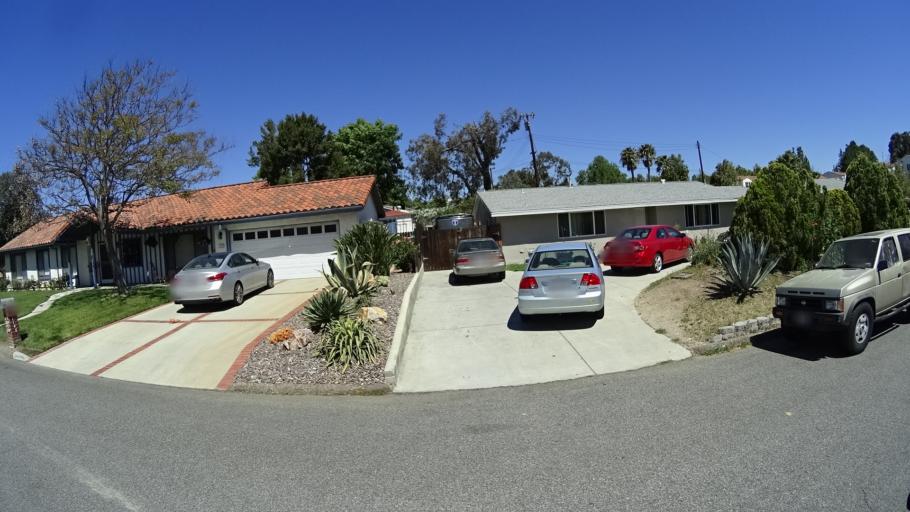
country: US
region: California
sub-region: Ventura County
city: Thousand Oaks
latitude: 34.1798
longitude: -118.8587
